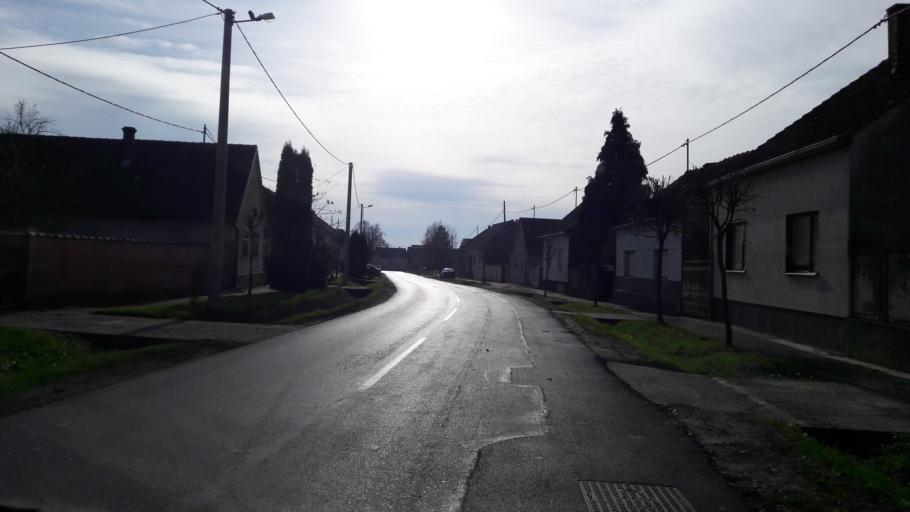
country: HR
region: Vukovarsko-Srijemska
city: Vodinci
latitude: 45.2879
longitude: 18.5590
